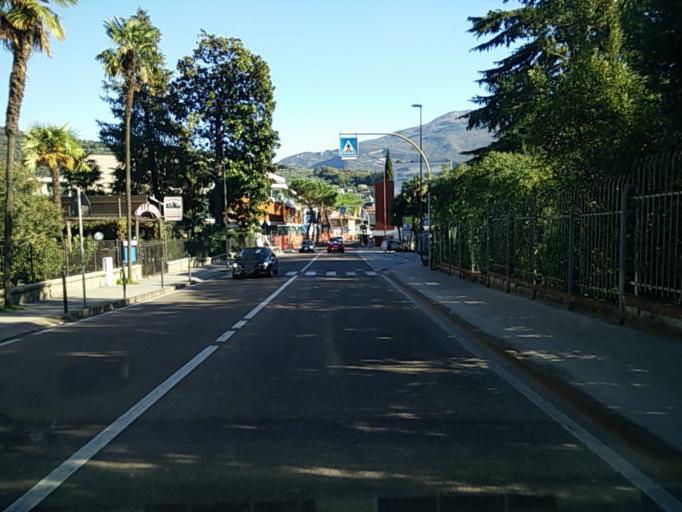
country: IT
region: Trentino-Alto Adige
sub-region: Provincia di Trento
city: Riva del Garda
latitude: 45.8834
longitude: 10.8521
